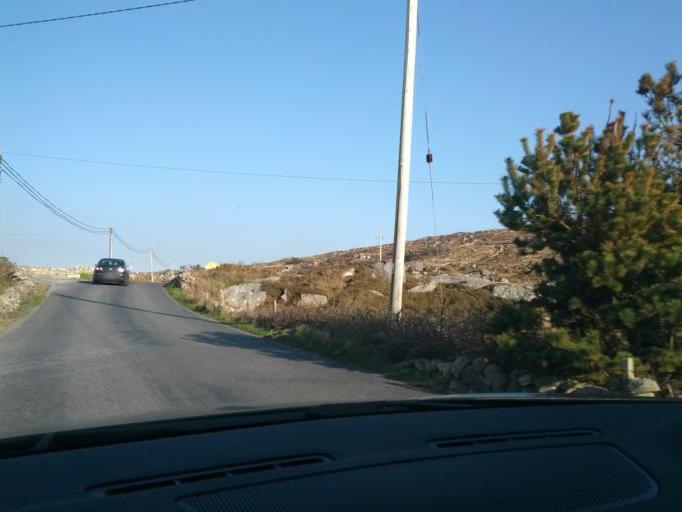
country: IE
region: Connaught
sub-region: County Galway
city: Clifden
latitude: 53.3373
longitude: -9.8637
